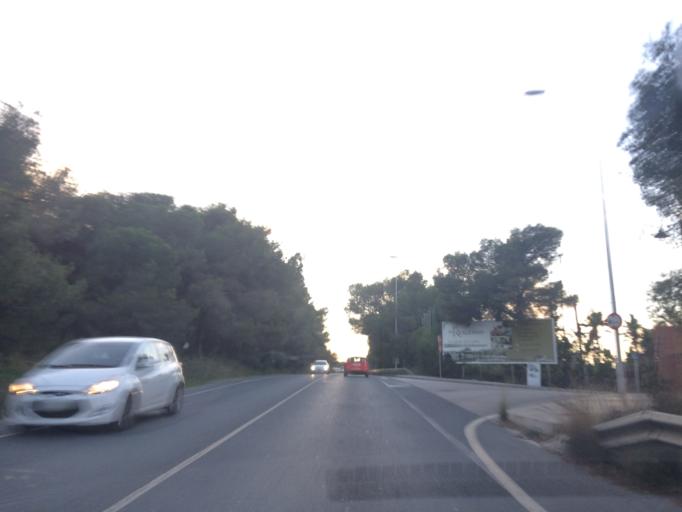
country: ES
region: Andalusia
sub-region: Provincia de Malaga
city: Alhaurin de la Torre
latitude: 36.6604
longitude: -4.5192
